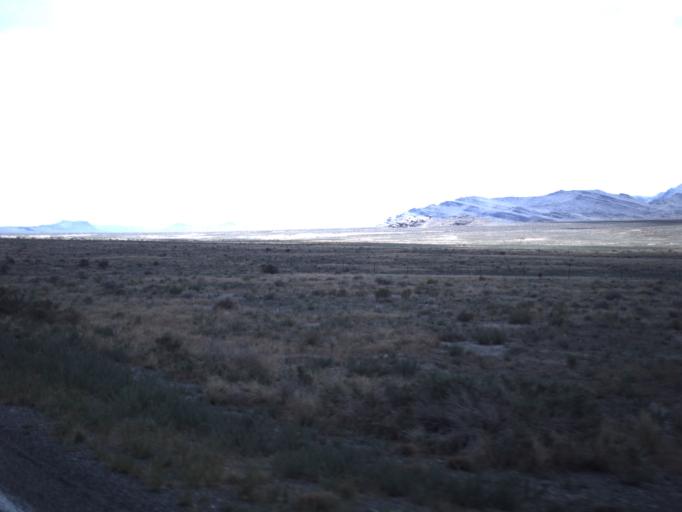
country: US
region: Utah
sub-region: Beaver County
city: Milford
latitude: 39.0438
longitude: -113.4069
